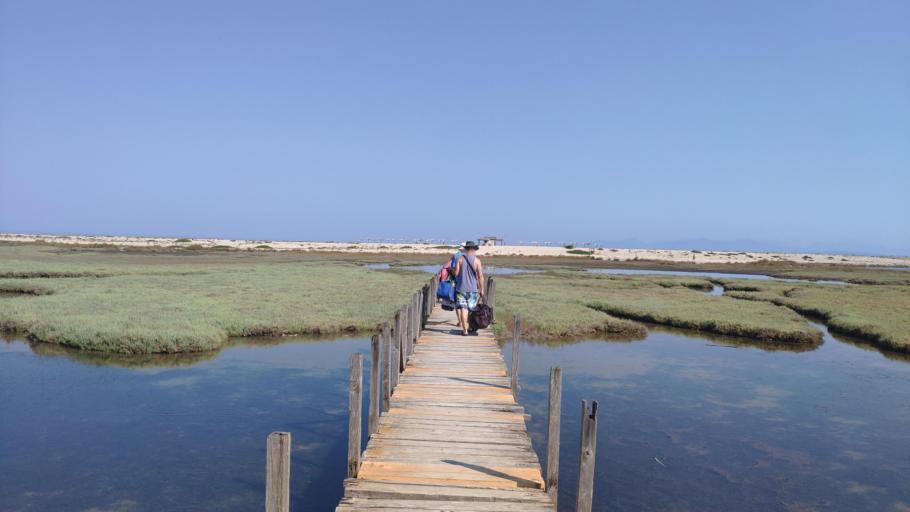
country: GR
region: Ionian Islands
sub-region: Lefkada
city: Lefkada
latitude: 38.8512
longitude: 20.7369
